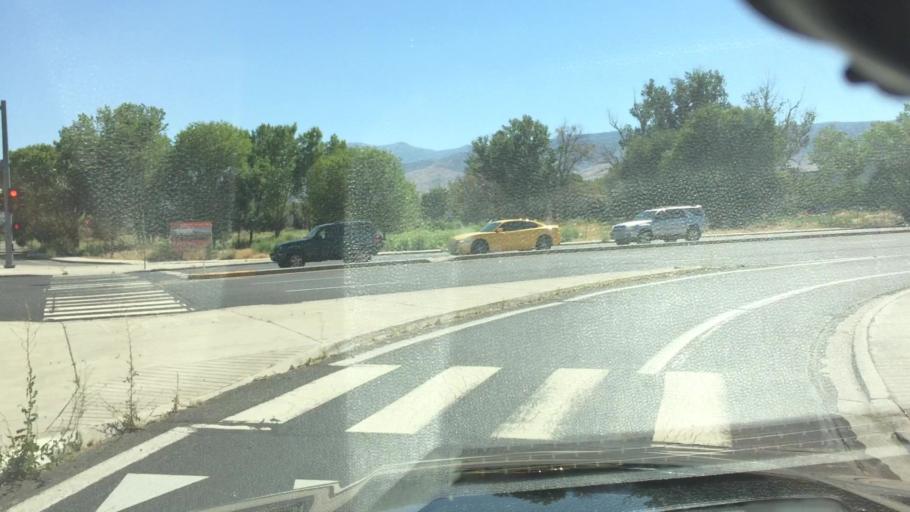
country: US
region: Nevada
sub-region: Washoe County
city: Sparks
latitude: 39.4686
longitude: -119.7687
